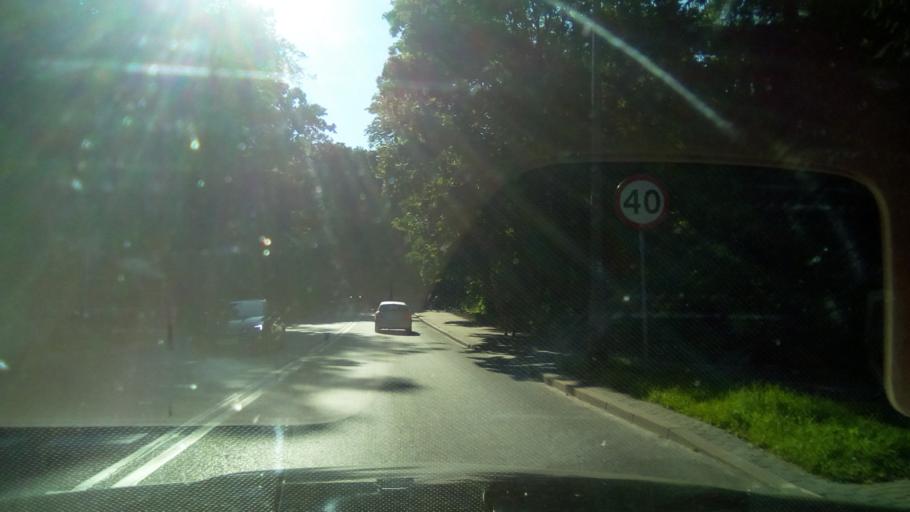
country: PL
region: Lublin Voivodeship
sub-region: Powiat pulawski
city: Pulawy
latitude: 51.4114
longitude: 21.9669
